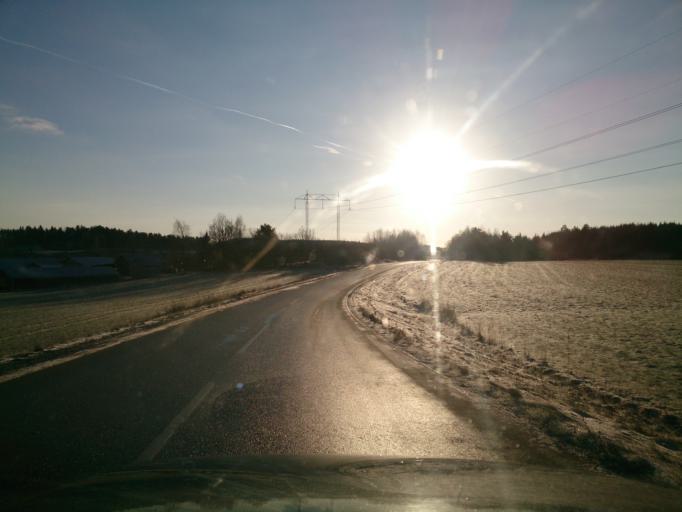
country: SE
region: OEstergoetland
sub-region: Norrkopings Kommun
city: Kimstad
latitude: 58.3717
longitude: 16.0246
